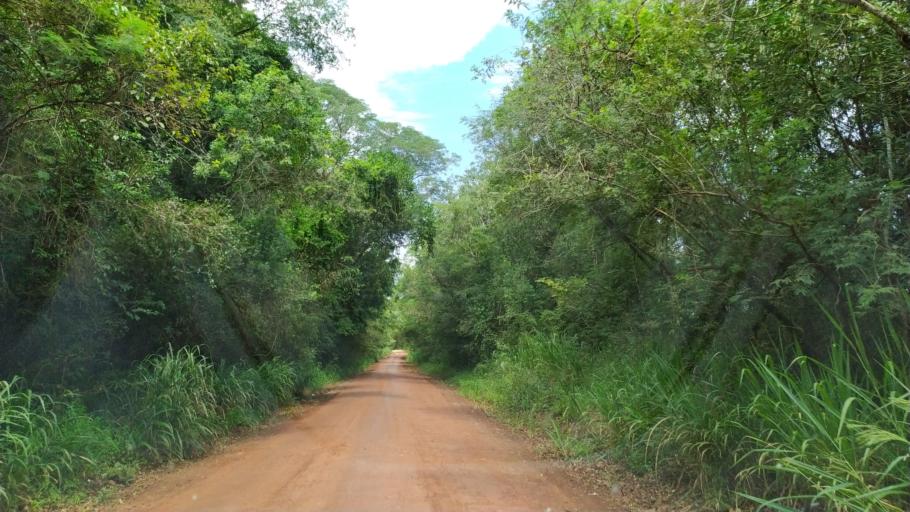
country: AR
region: Misiones
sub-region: Departamento de Eldorado
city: Eldorado
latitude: -26.4770
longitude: -54.5929
